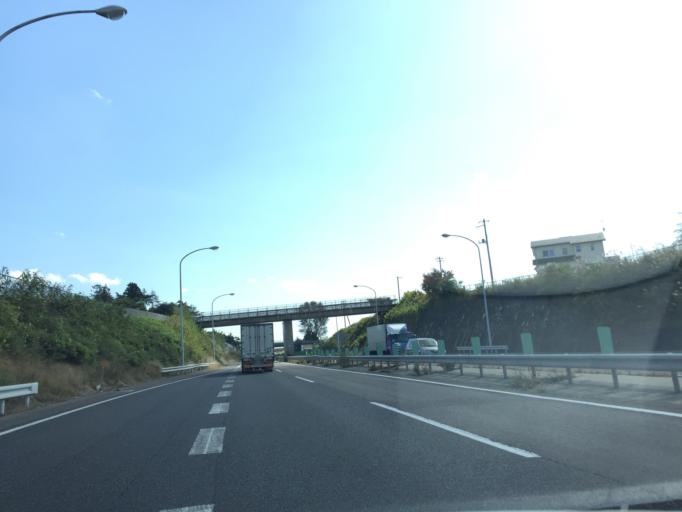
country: JP
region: Fukushima
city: Koriyama
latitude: 37.3519
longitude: 140.3248
